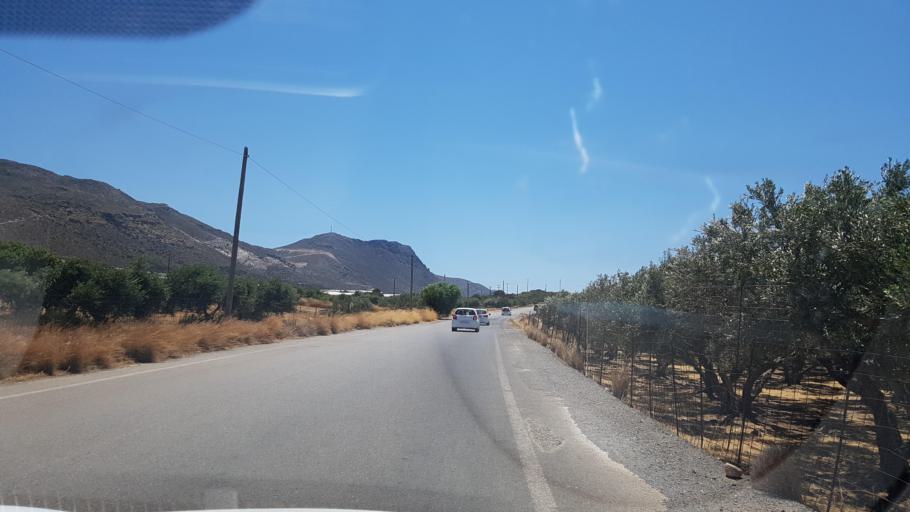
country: GR
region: Crete
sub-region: Nomos Chanias
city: Palaiochora
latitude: 35.2898
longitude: 23.5473
